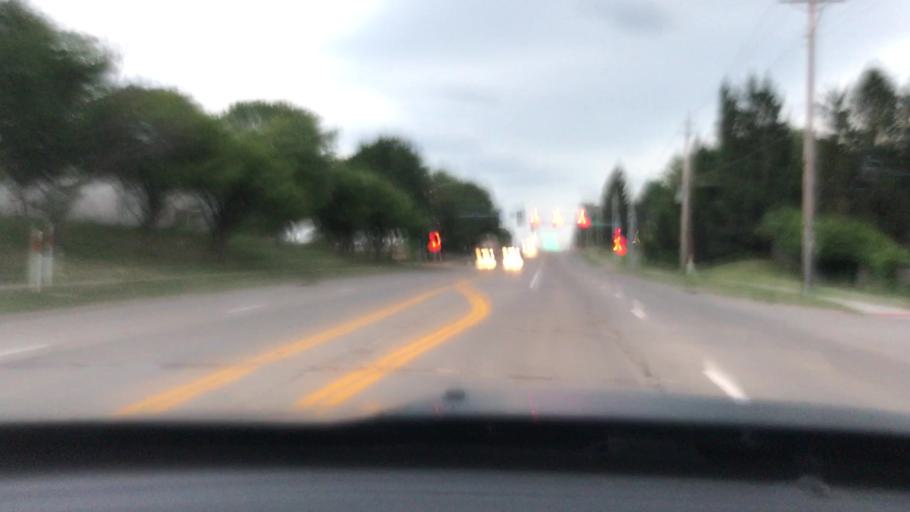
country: US
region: Iowa
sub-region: Scott County
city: Bettendorf
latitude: 41.5748
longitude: -90.5375
